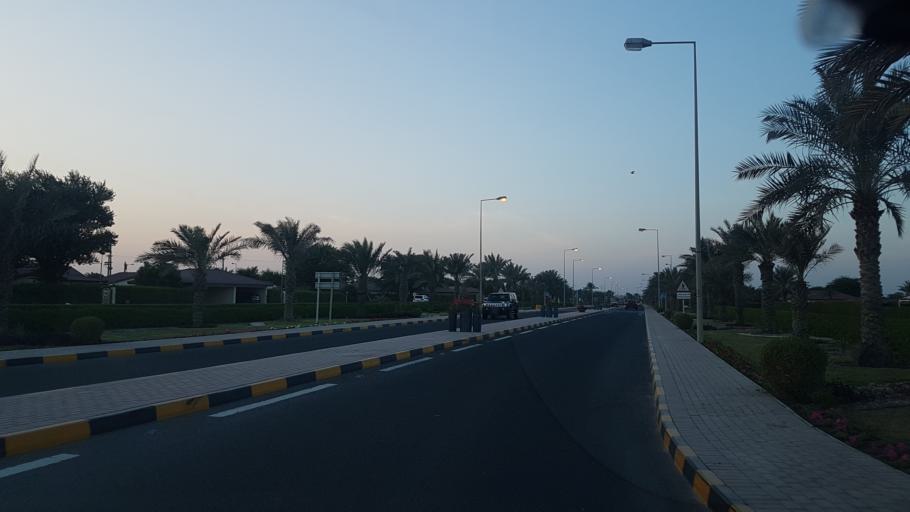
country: BH
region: Northern
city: Ar Rifa'
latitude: 26.0929
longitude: 50.5476
